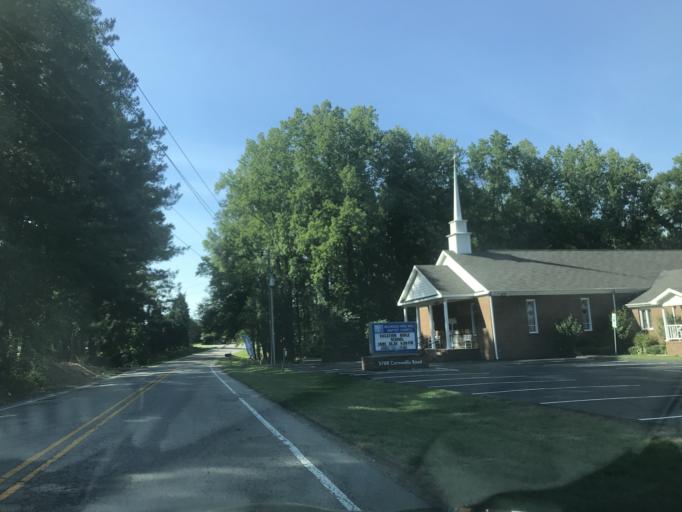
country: US
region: North Carolina
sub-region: Johnston County
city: Clayton
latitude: 35.6210
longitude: -78.5366
